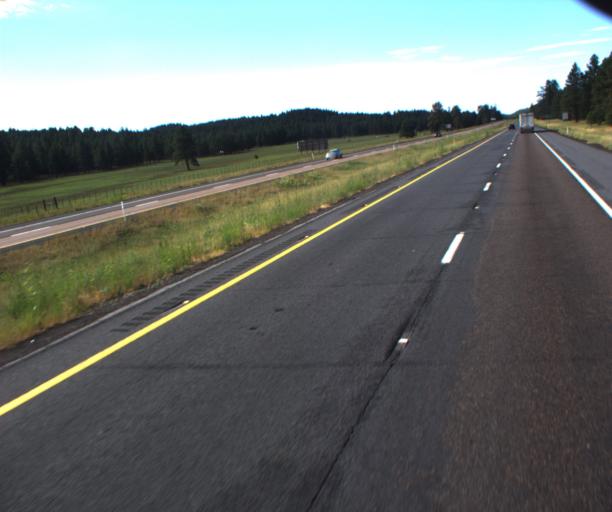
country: US
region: Arizona
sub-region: Coconino County
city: Mountainaire
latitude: 35.0096
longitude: -111.6855
